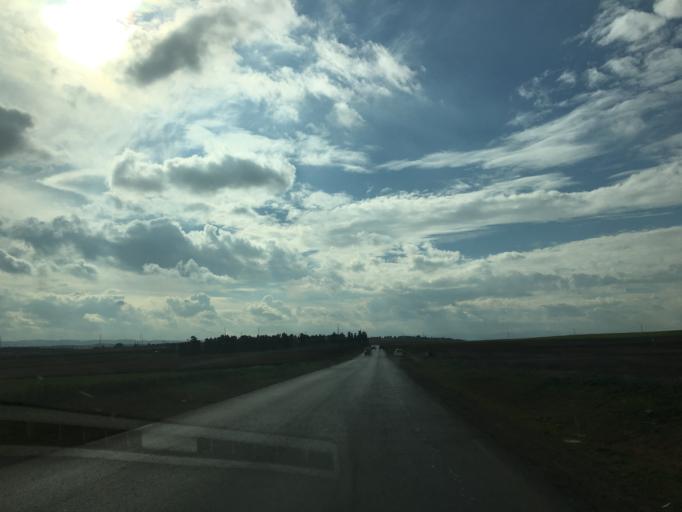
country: DZ
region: Bouira
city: Bouira
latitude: 36.3243
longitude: 3.8701
